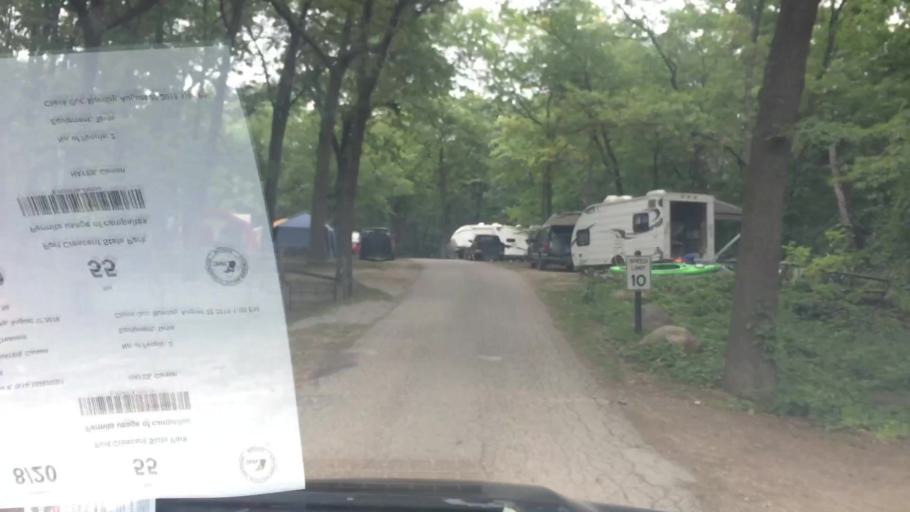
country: US
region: Michigan
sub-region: Huron County
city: Bad Axe
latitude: 44.0090
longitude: -83.0514
